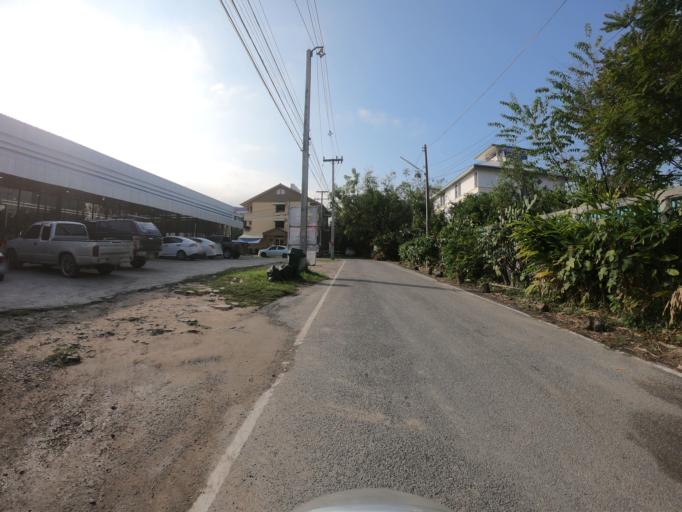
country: TH
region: Chiang Mai
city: Chiang Mai
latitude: 18.8099
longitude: 98.9671
